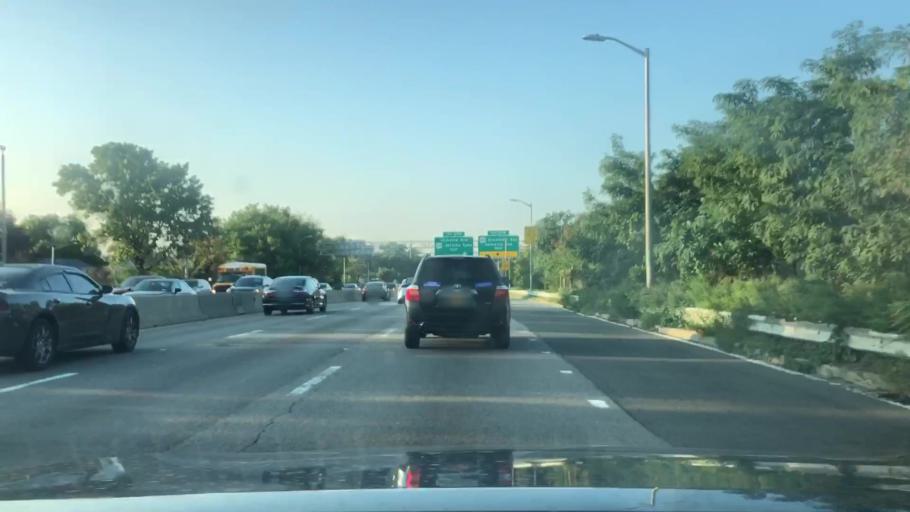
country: US
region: New York
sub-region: Nassau County
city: Bellerose Terrace
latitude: 40.7295
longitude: -73.7236
